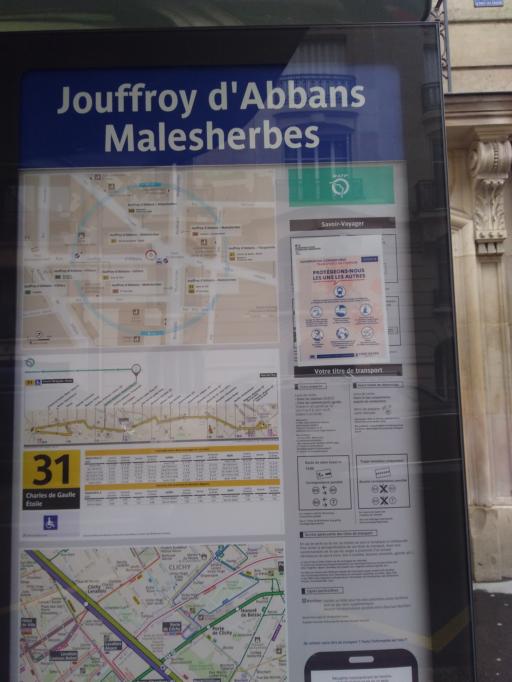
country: FR
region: Ile-de-France
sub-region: Departement des Hauts-de-Seine
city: Clichy
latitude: 48.8848
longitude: 2.3065
